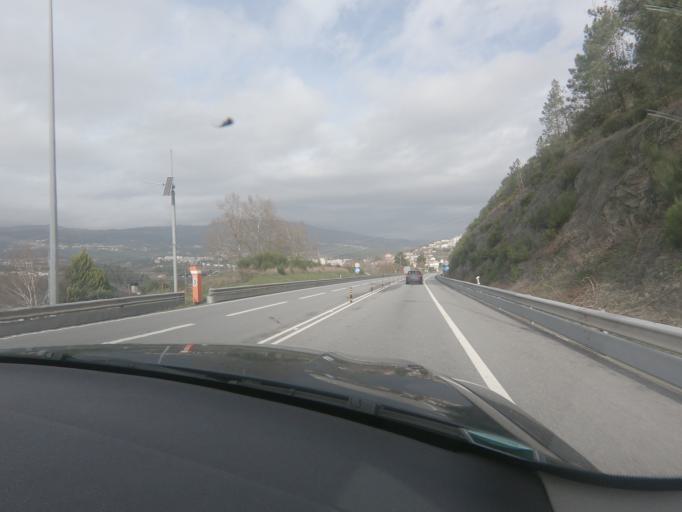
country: PT
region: Vila Real
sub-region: Vila Real
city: Vila Real
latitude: 41.2892
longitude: -7.7575
